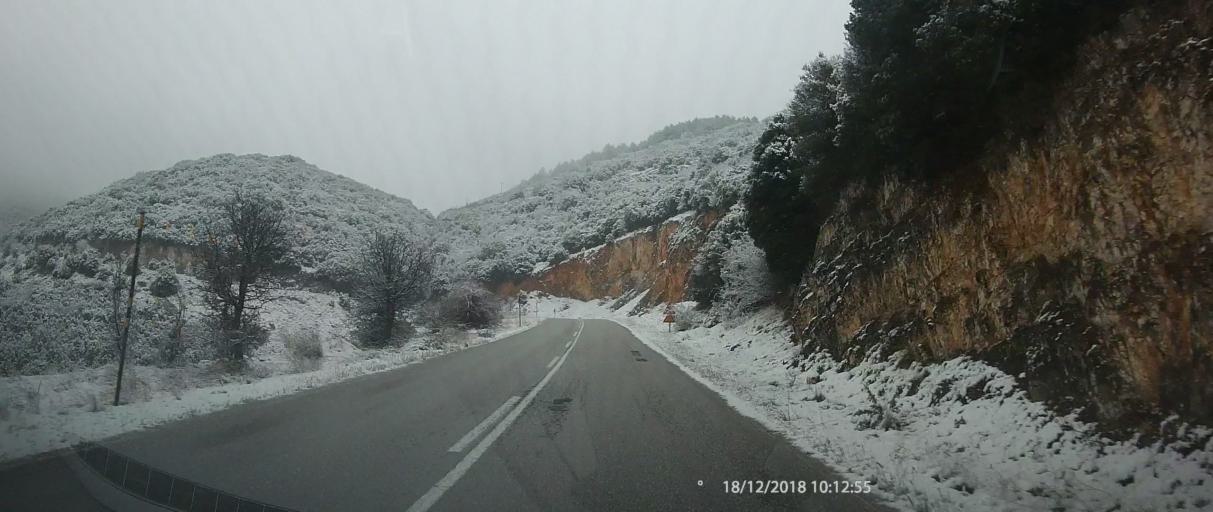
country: GR
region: Thessaly
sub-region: Nomos Larisis
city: Livadi
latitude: 40.1027
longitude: 22.2106
